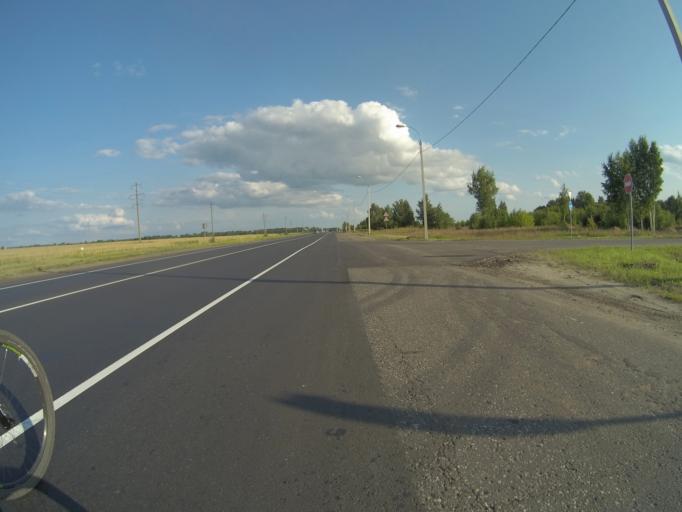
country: RU
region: Vladimir
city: Suzdal'
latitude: 56.4446
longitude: 40.4649
